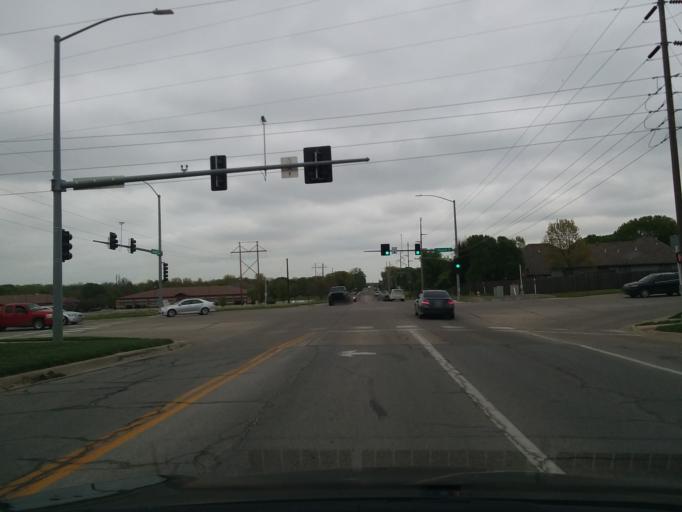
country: US
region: Kansas
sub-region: Douglas County
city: Lawrence
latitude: 38.9861
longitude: -95.2796
